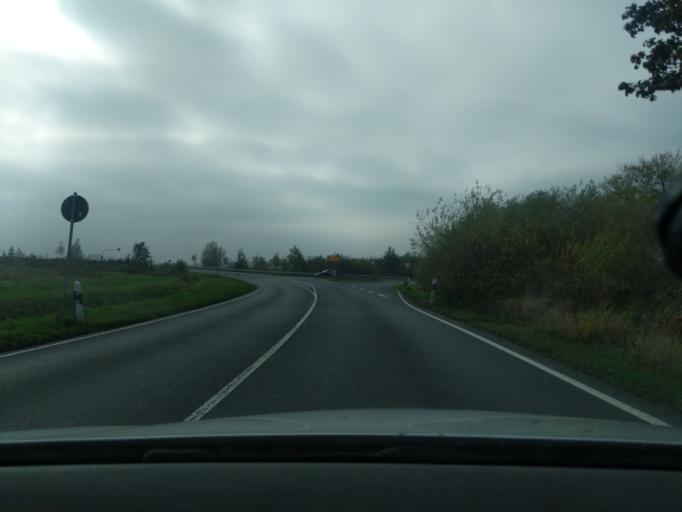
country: DE
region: Lower Saxony
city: Otterndorf
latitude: 53.8150
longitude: 8.9235
